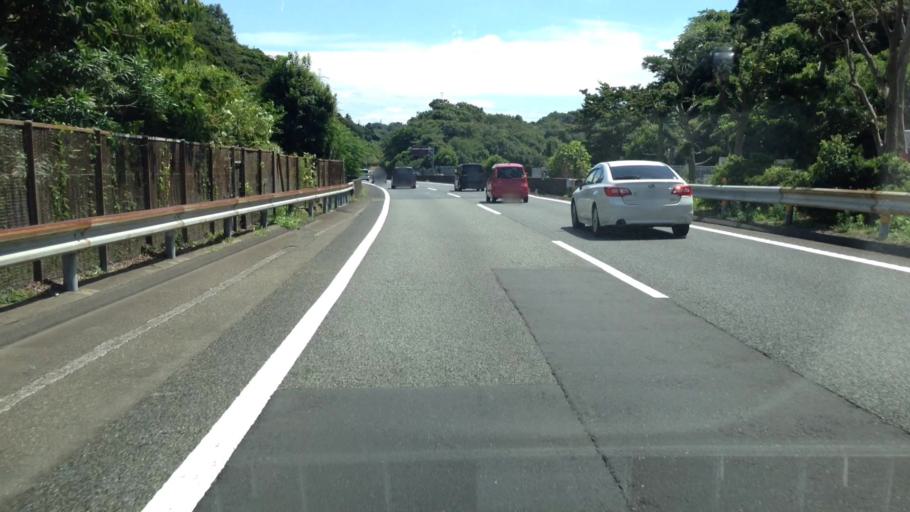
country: JP
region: Kanagawa
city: Zushi
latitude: 35.3042
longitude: 139.6110
